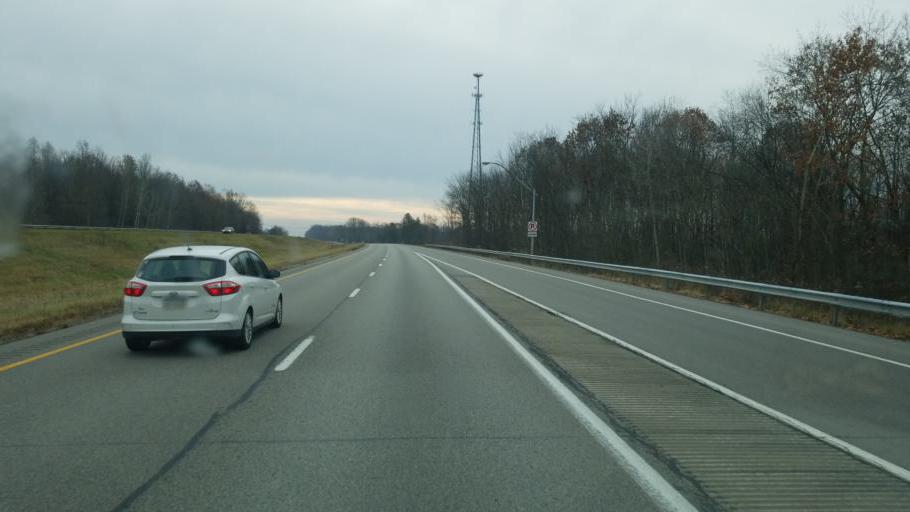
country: US
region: Pennsylvania
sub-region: Crawford County
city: Cochranton
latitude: 41.4656
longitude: -80.1670
